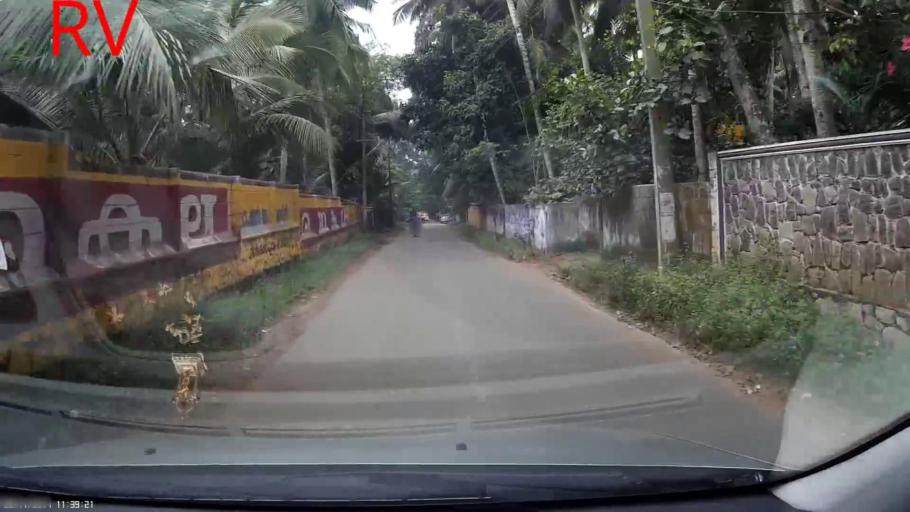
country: IN
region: Kerala
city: Kovalam
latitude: 8.3958
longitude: 77.0248
